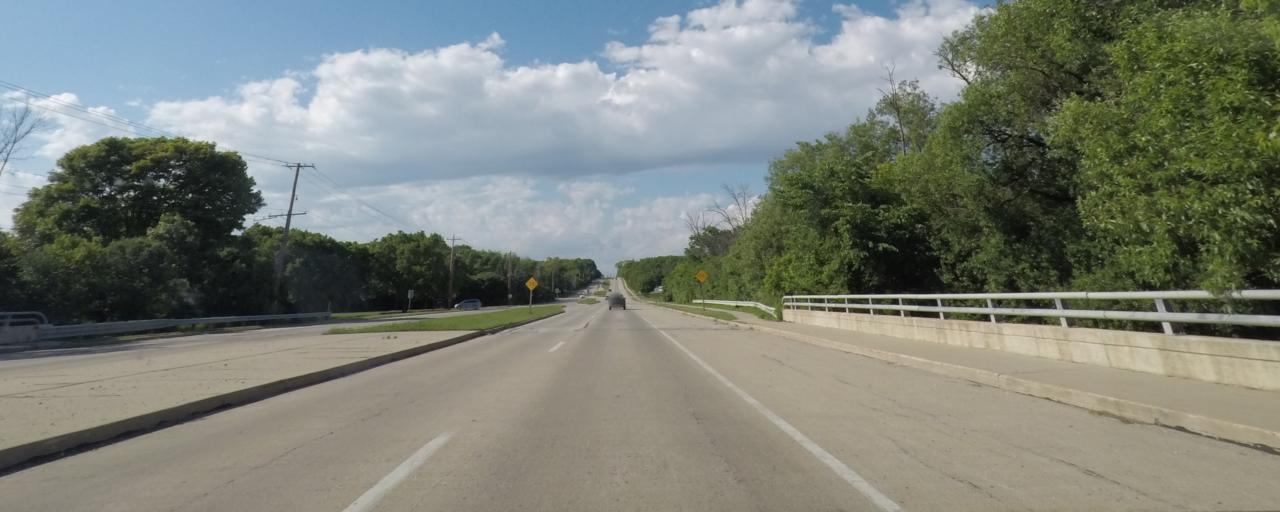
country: US
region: Wisconsin
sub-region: Milwaukee County
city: Greendale
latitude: 42.9277
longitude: -88.0088
